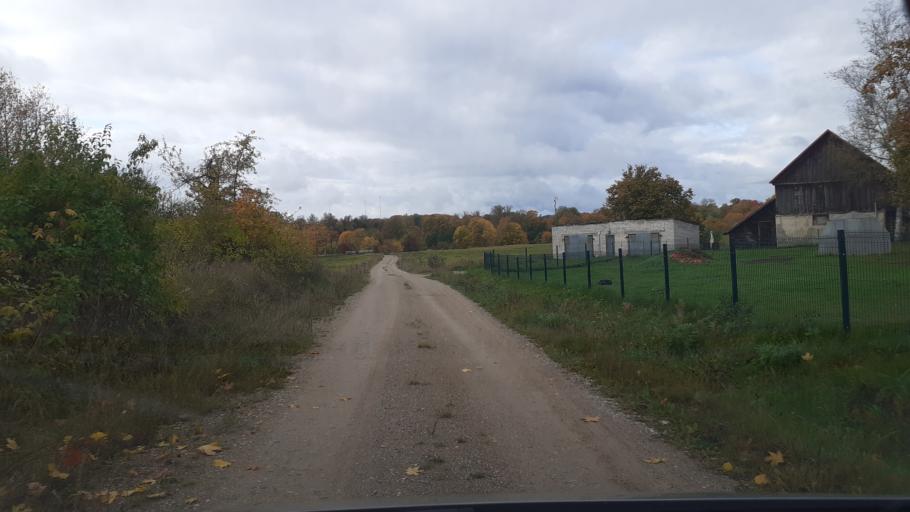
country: LV
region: Kuldigas Rajons
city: Kuldiga
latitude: 56.9708
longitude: 21.9877
